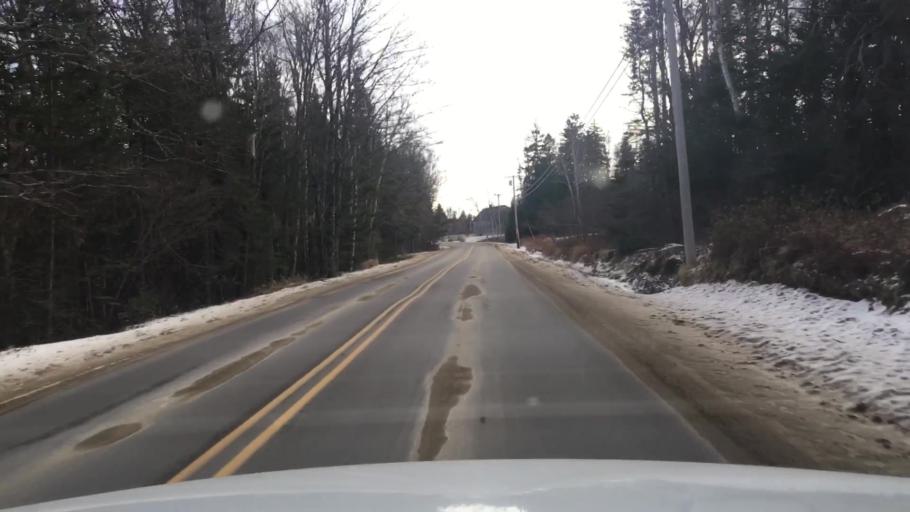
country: US
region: Maine
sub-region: Washington County
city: Jonesport
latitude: 44.6113
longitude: -67.6021
